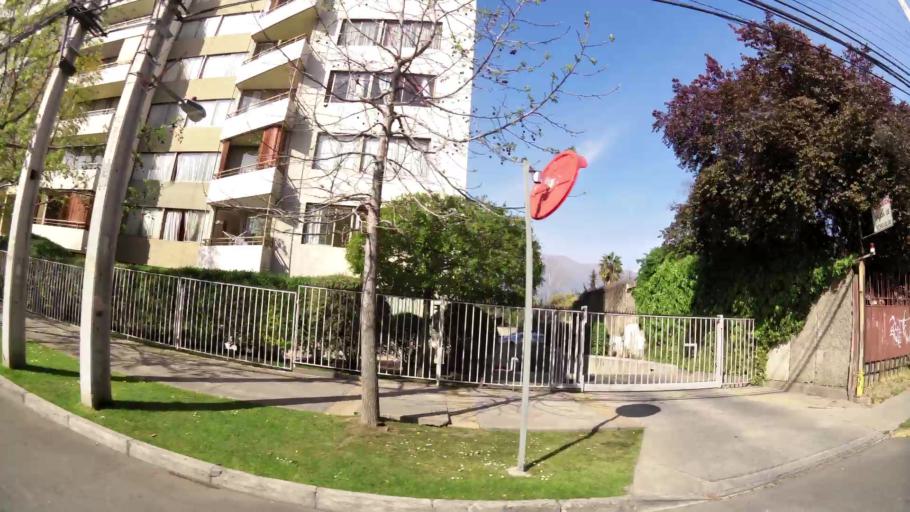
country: CL
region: Santiago Metropolitan
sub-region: Provincia de Santiago
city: Villa Presidente Frei, Nunoa, Santiago, Chile
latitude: -33.5250
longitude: -70.5892
